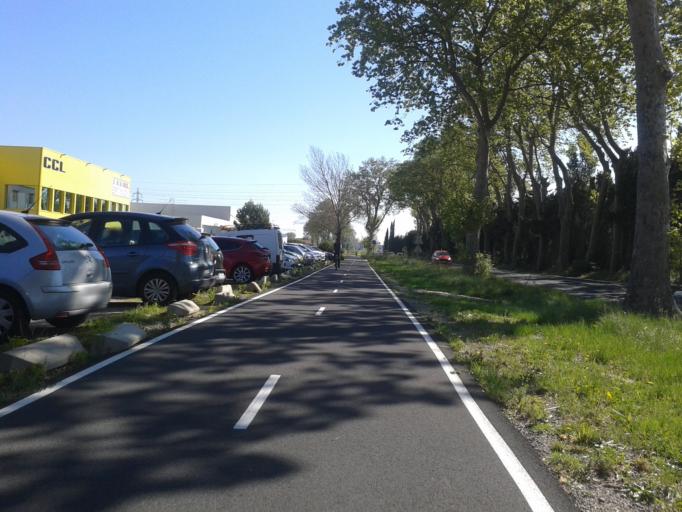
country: FR
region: Languedoc-Roussillon
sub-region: Departement des Pyrenees-Orientales
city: Toulouges
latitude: 42.6763
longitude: 2.8441
